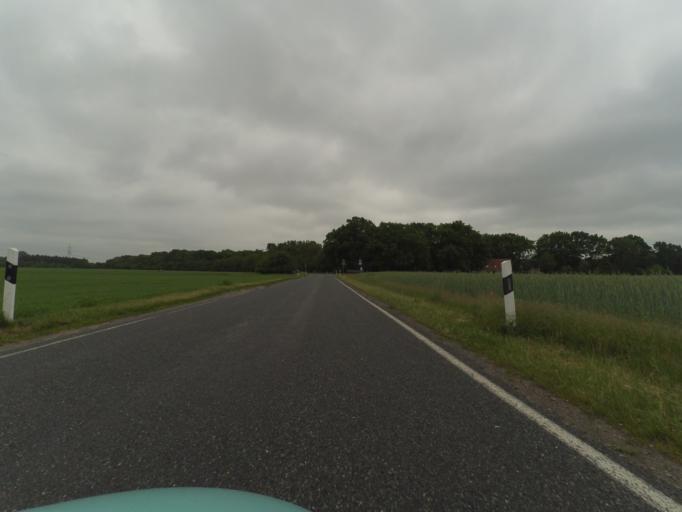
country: DE
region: Lower Saxony
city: Edemissen
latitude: 52.4430
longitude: 10.2777
